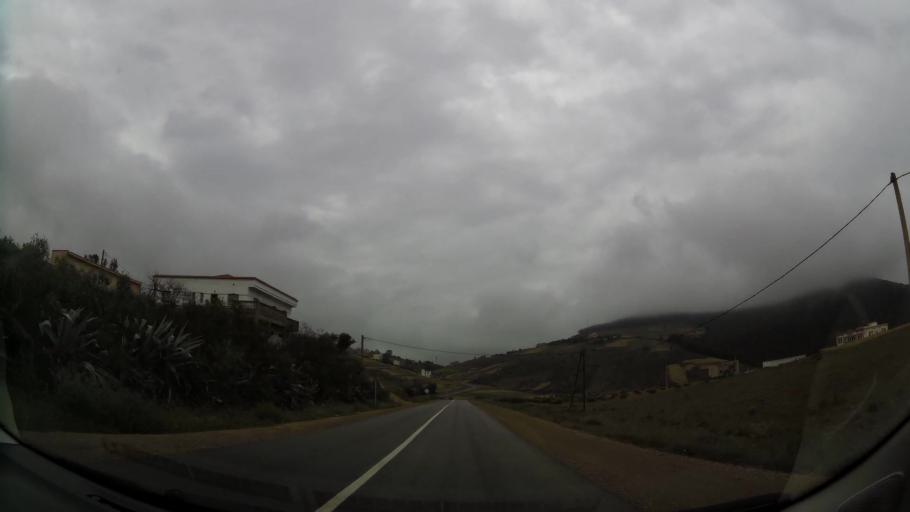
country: MA
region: Oriental
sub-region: Nador
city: Nador
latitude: 35.1383
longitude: -3.0516
